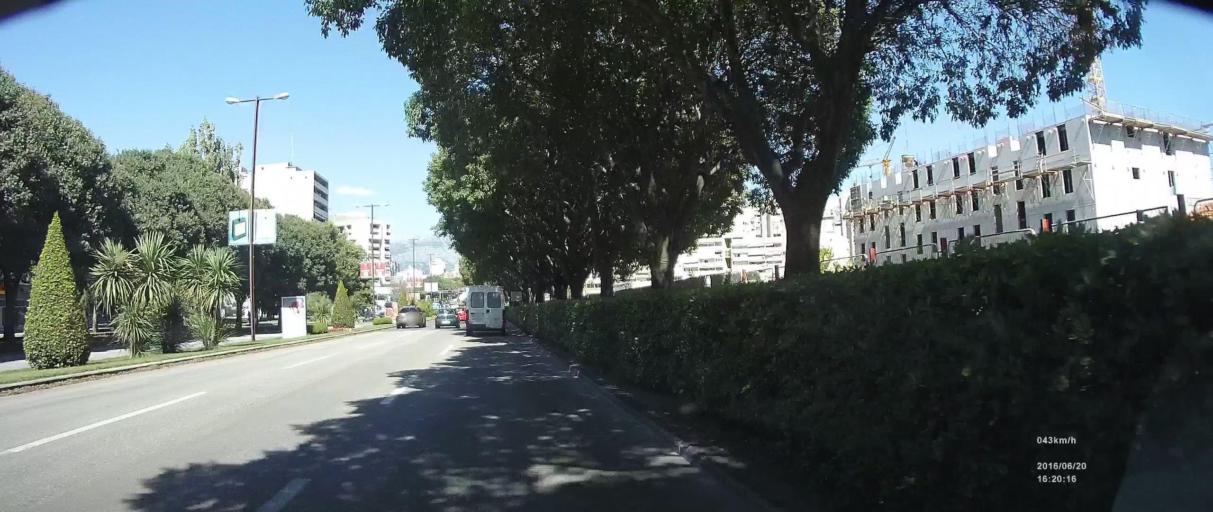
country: HR
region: Splitsko-Dalmatinska
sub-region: Grad Split
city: Split
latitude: 43.5061
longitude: 16.4621
